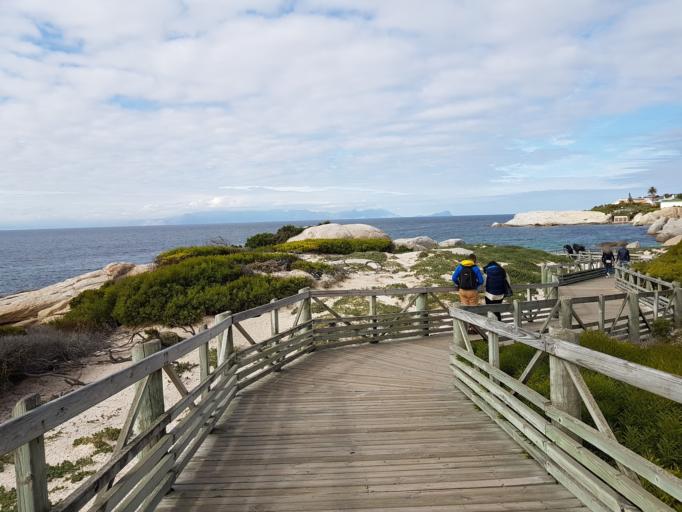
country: ZA
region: Western Cape
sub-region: City of Cape Town
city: Retreat
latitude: -34.1955
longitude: 18.4500
